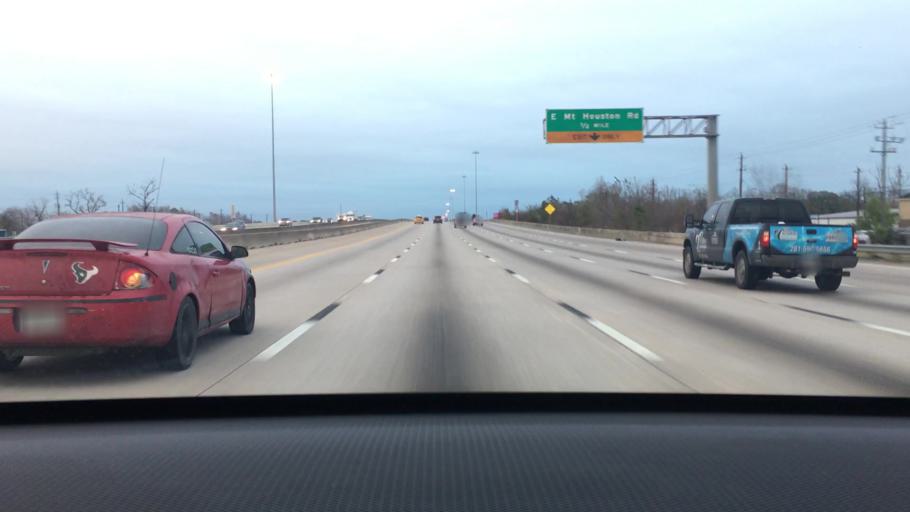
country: US
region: Texas
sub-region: Harris County
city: Aldine
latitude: 29.8764
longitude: -95.3263
